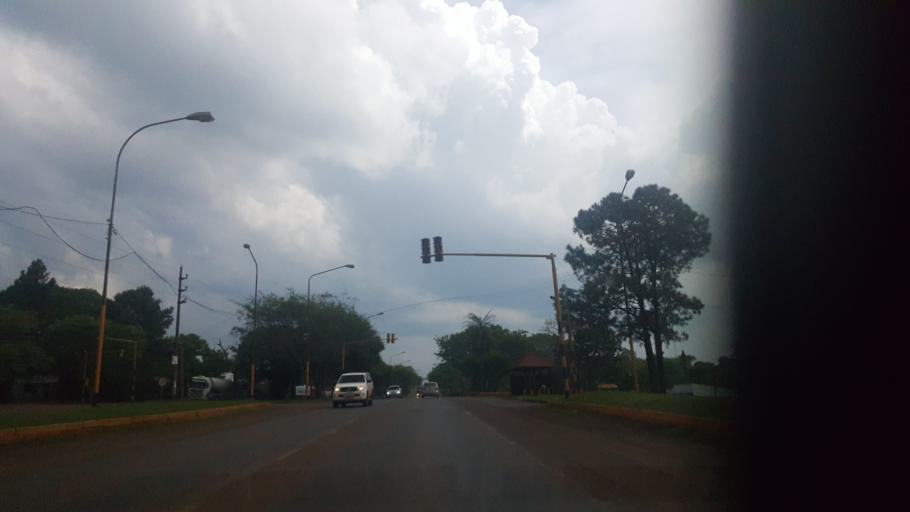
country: AR
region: Misiones
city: Jardin America
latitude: -27.0432
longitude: -55.2348
